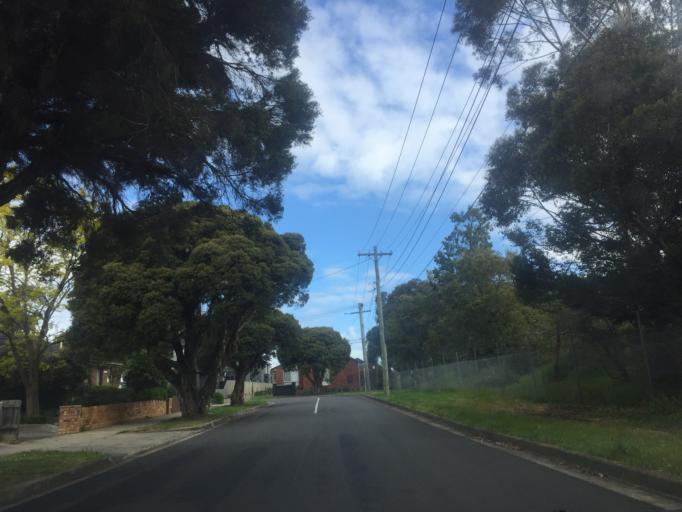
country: AU
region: Victoria
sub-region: Darebin
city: Reservoir
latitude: -37.7228
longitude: 145.0110
